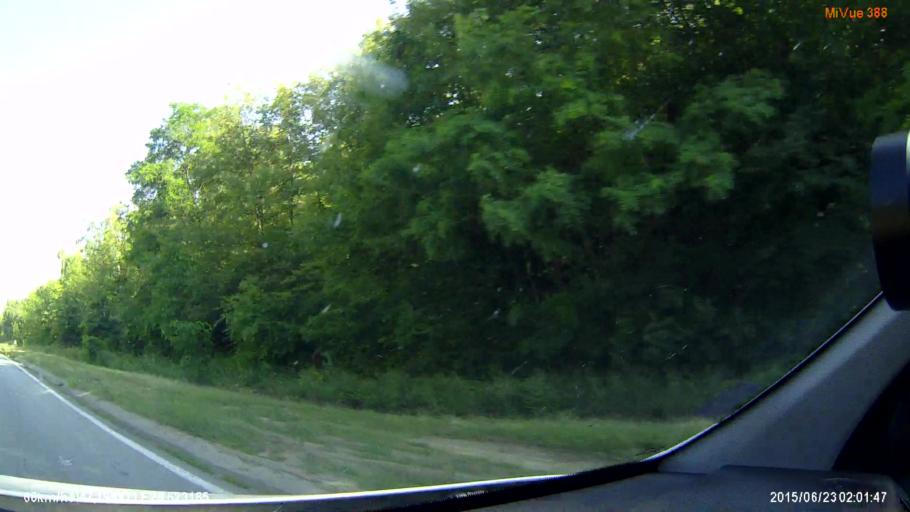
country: MD
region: Straseni
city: Straseni
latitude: 47.1999
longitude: 28.6228
